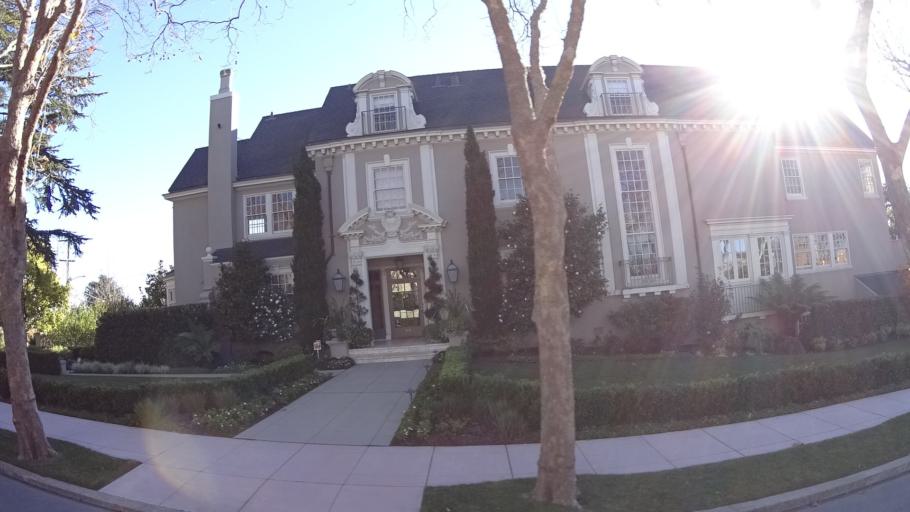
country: US
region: California
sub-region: Alameda County
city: Piedmont
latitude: 37.8165
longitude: -122.2245
